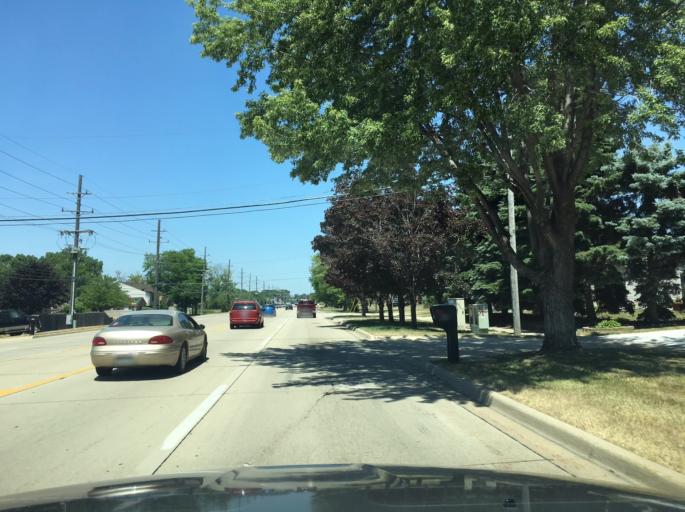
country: US
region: Michigan
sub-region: Macomb County
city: Fraser
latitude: 42.5598
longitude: -82.9505
